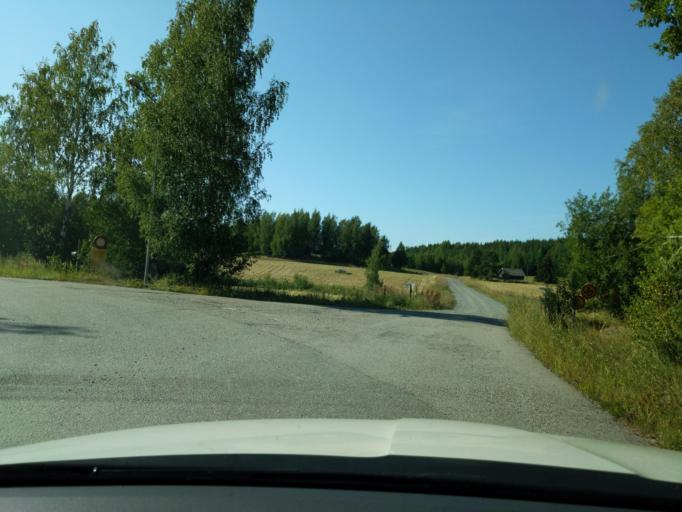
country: FI
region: Uusimaa
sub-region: Raaseporin
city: Inga
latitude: 60.0201
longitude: 23.9214
